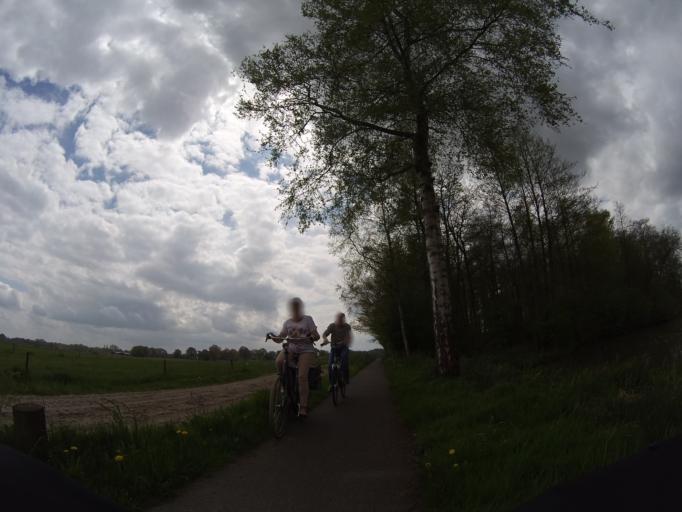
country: NL
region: Overijssel
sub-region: Gemeente Hardenberg
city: Hardenberg
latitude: 52.5338
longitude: 6.5738
